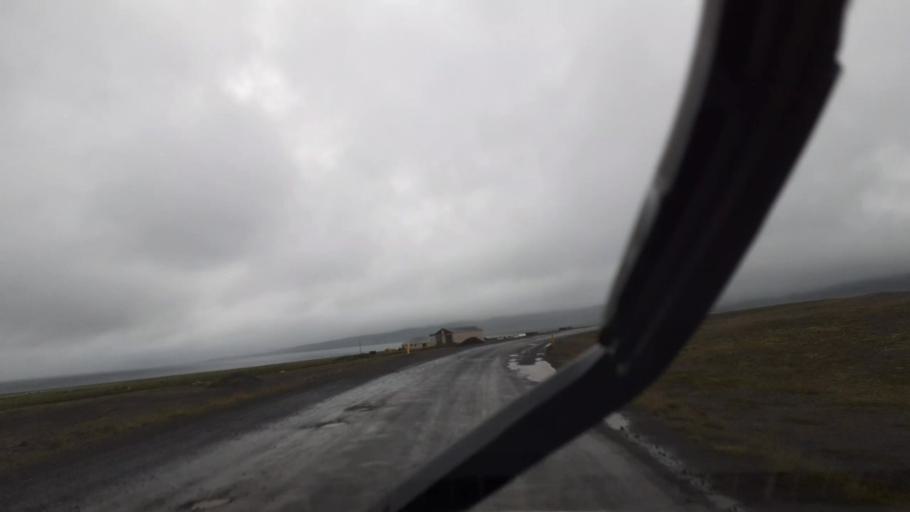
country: IS
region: East
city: Egilsstadir
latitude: 66.0692
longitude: -15.0880
